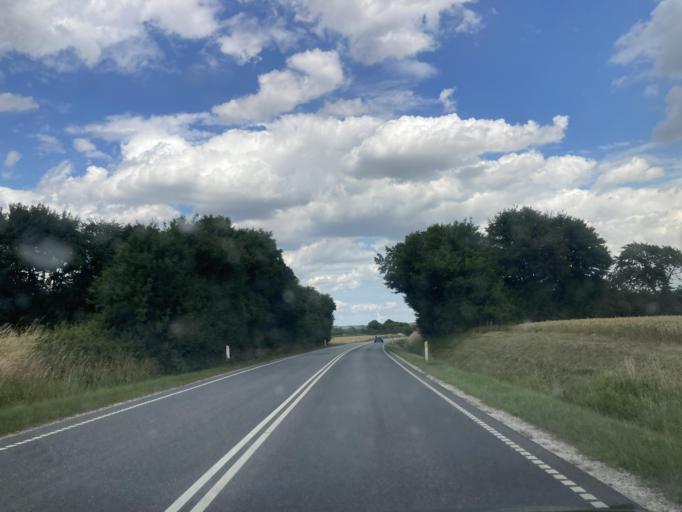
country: DK
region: Zealand
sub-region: Faxe Kommune
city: Haslev
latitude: 55.3391
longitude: 12.0325
